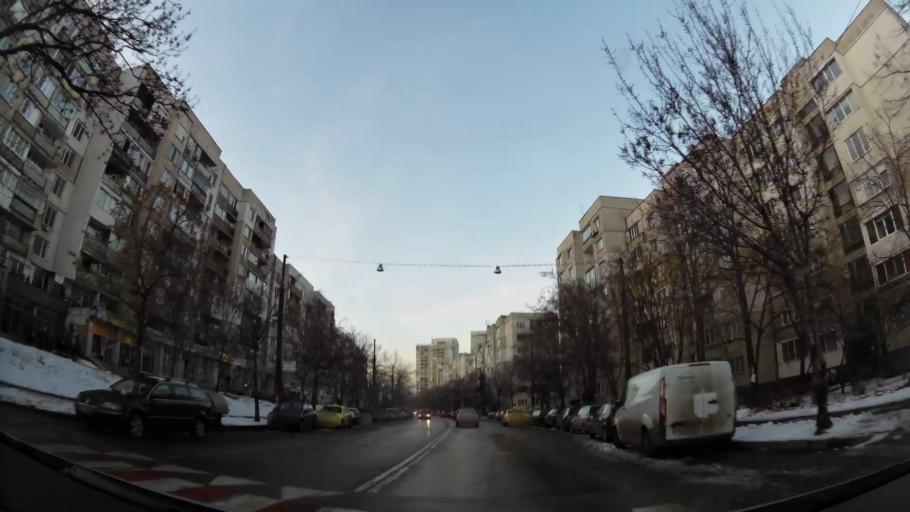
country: BG
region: Sofia-Capital
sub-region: Stolichna Obshtina
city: Sofia
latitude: 42.6870
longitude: 23.3716
